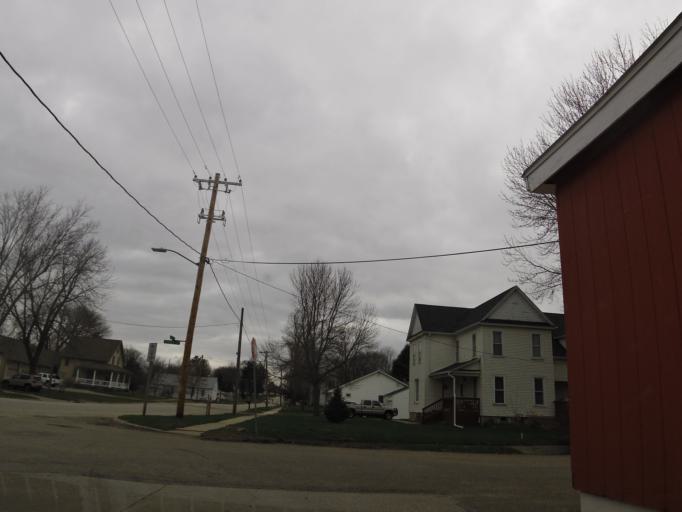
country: US
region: Iowa
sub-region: Benton County
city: Vinton
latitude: 42.3145
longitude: -92.0033
